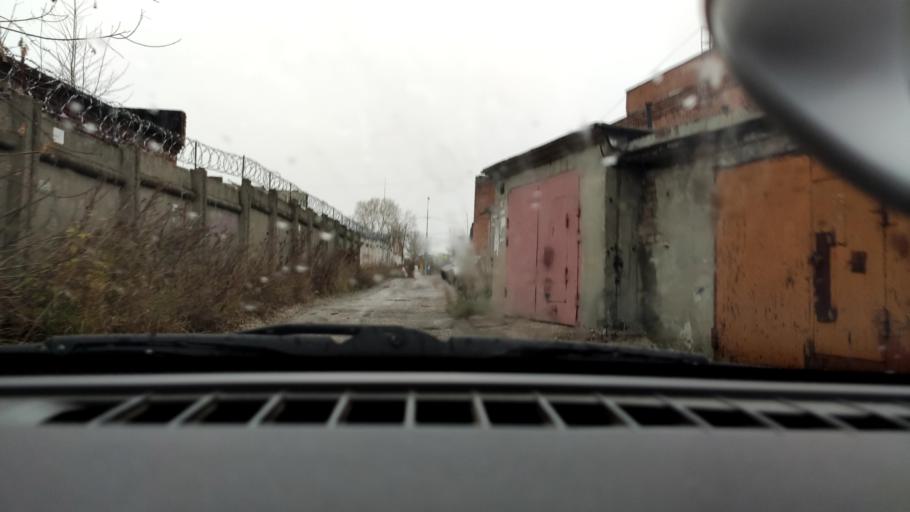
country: RU
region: Perm
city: Kondratovo
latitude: 57.9595
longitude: 56.1661
